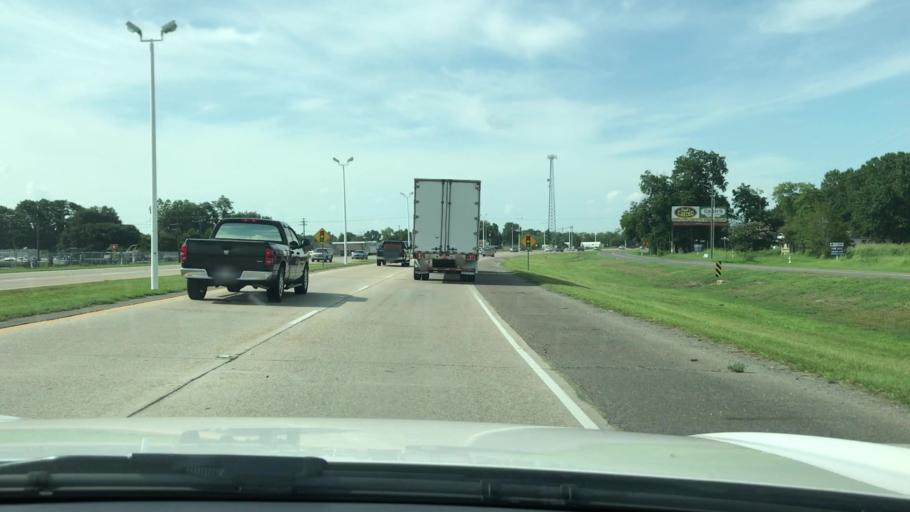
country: US
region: Louisiana
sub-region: West Baton Rouge Parish
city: Addis
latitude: 30.3617
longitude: -91.2609
